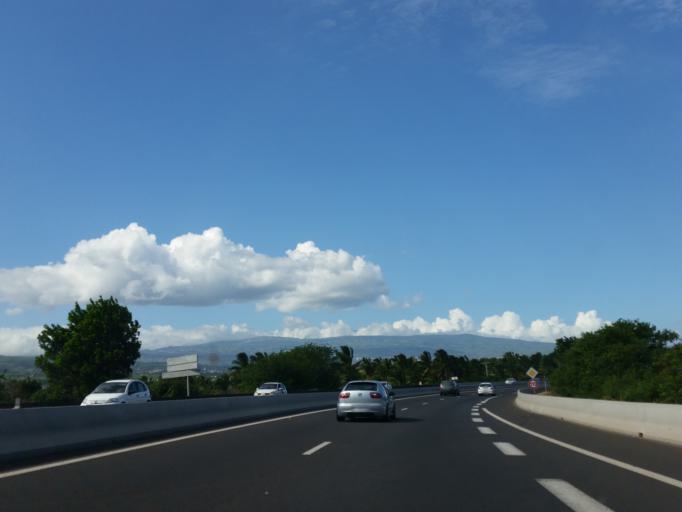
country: RE
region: Reunion
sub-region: Reunion
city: Saint-Louis
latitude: -21.2787
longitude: 55.3811
